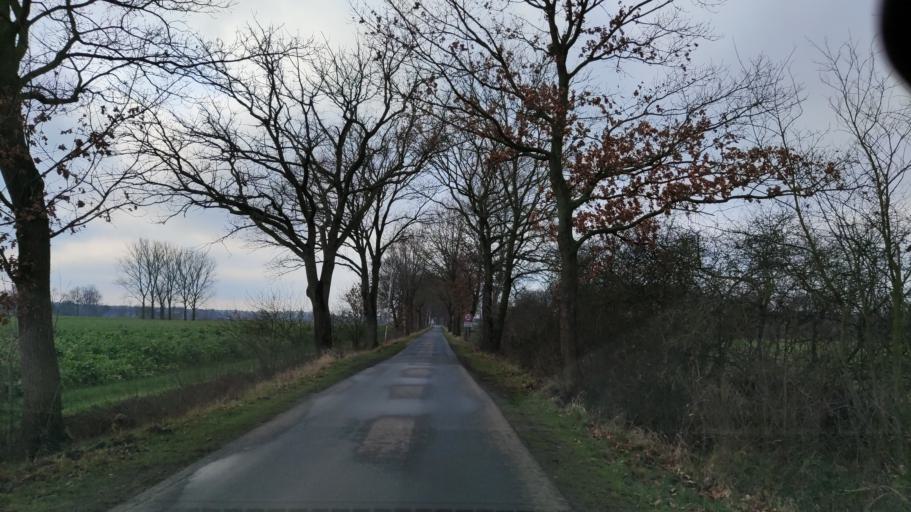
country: DE
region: Lower Saxony
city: Ludersburg
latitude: 53.3043
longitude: 10.6030
